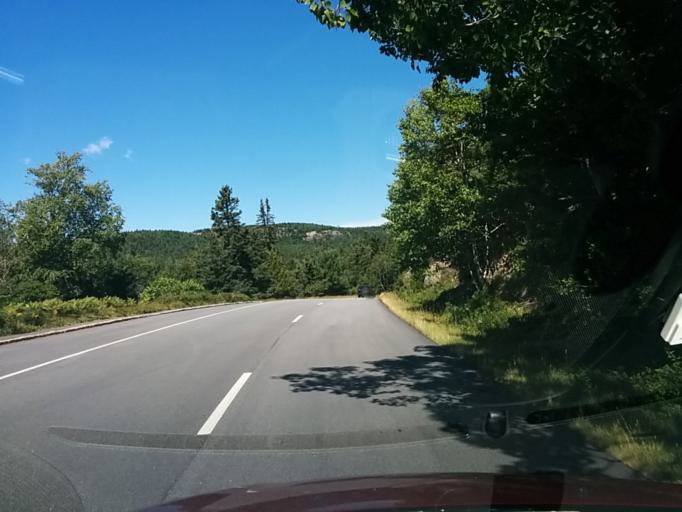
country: US
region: Maine
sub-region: Hancock County
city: Bar Harbor
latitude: 44.2977
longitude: -68.2154
